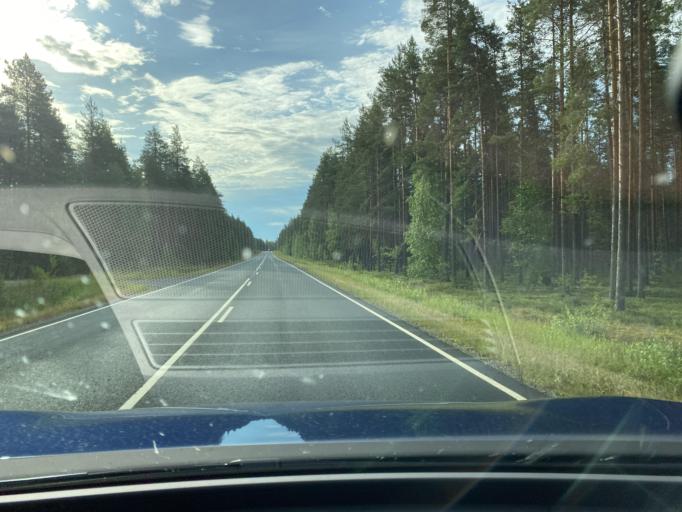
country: FI
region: Central Ostrobothnia
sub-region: Kaustinen
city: Veteli
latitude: 63.4101
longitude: 23.9632
